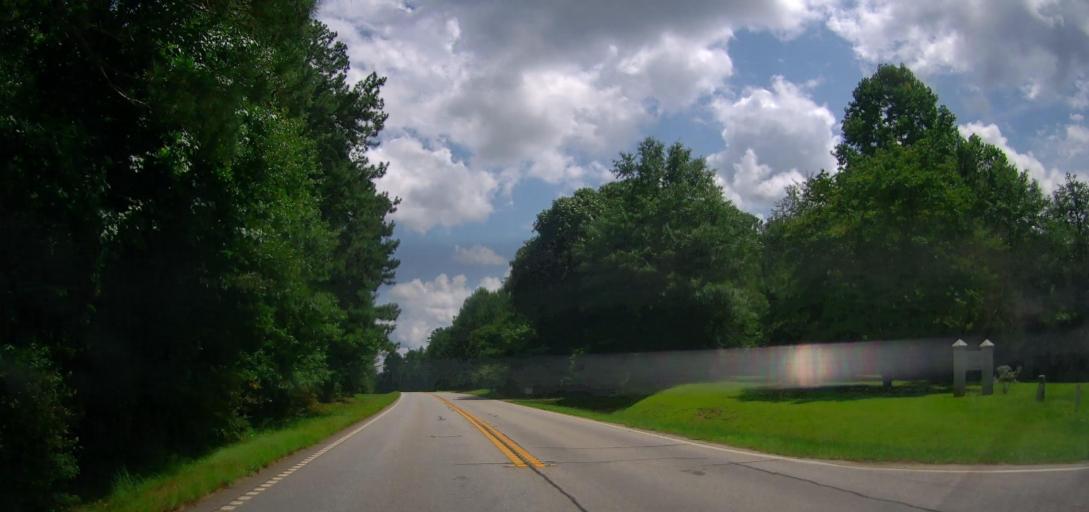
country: US
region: Georgia
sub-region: Heard County
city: Franklin
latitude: 33.3224
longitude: -85.1572
